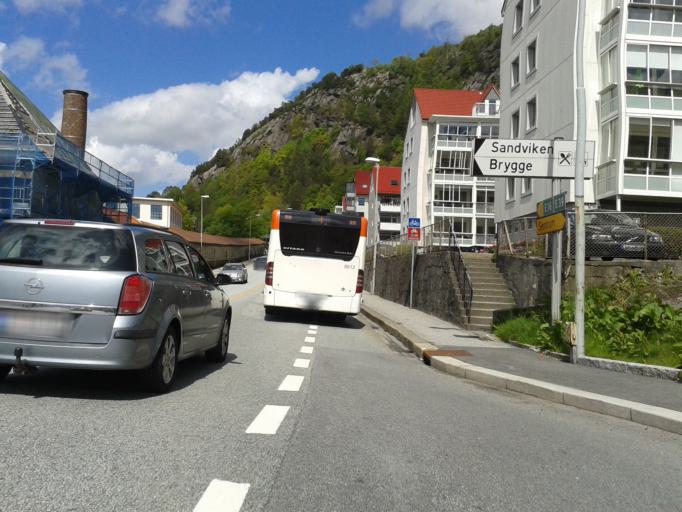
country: NO
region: Hordaland
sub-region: Bergen
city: Bergen
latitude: 60.4119
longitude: 5.3232
